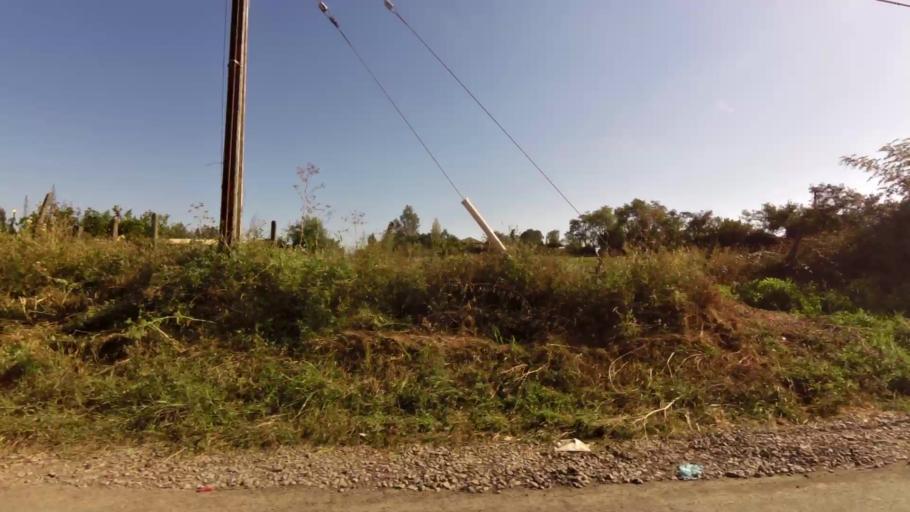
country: CL
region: Maule
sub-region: Provincia de Talca
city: Talca
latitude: -35.4005
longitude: -71.6123
